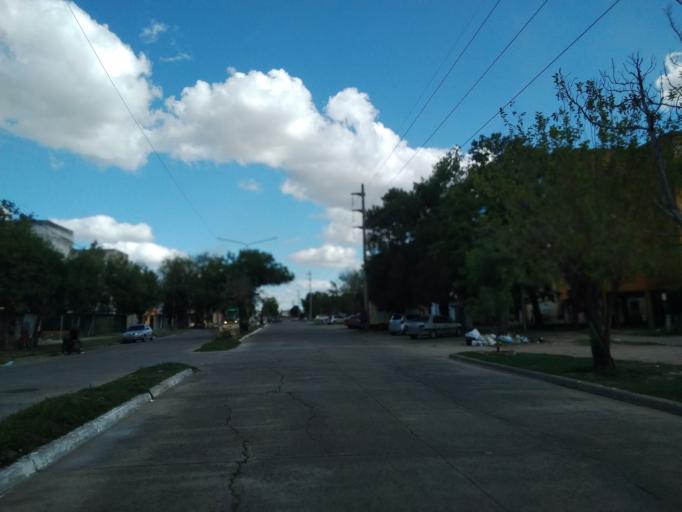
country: AR
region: Corrientes
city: Corrientes
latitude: -27.4962
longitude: -58.8270
